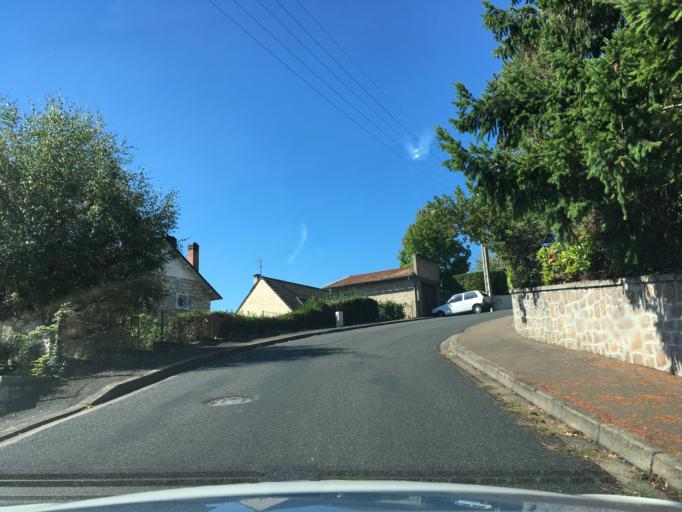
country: FR
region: Limousin
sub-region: Departement de la Correze
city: Brive-la-Gaillarde
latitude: 45.1672
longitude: 1.5198
